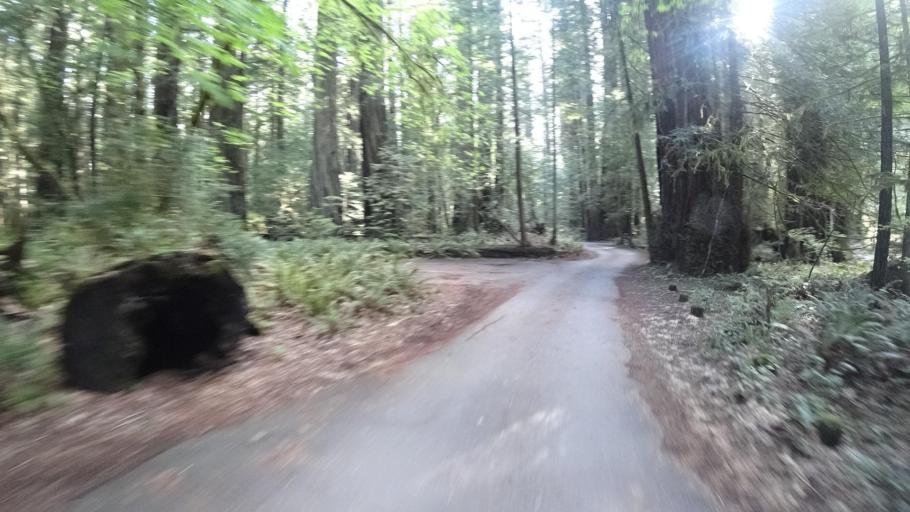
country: US
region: California
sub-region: Humboldt County
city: Rio Dell
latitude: 40.3506
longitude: -123.9922
